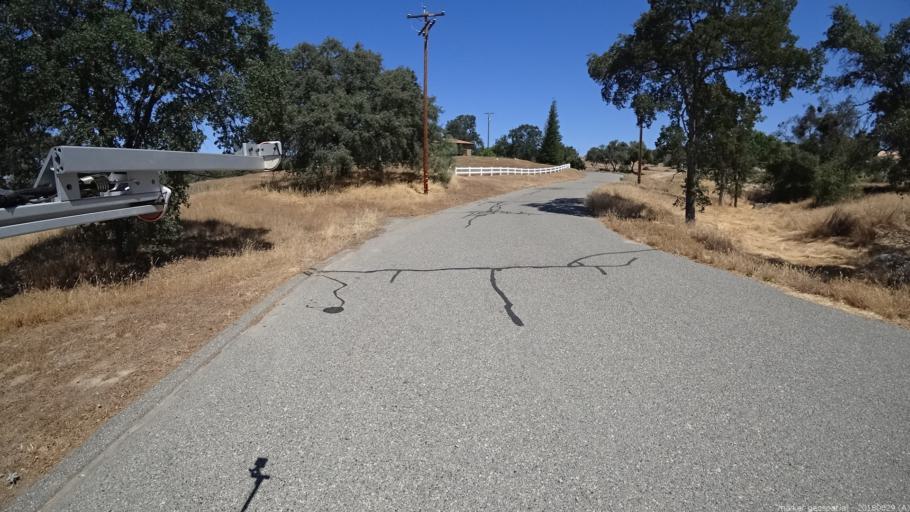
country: US
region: California
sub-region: Madera County
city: Yosemite Lakes
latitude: 37.1632
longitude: -119.7534
